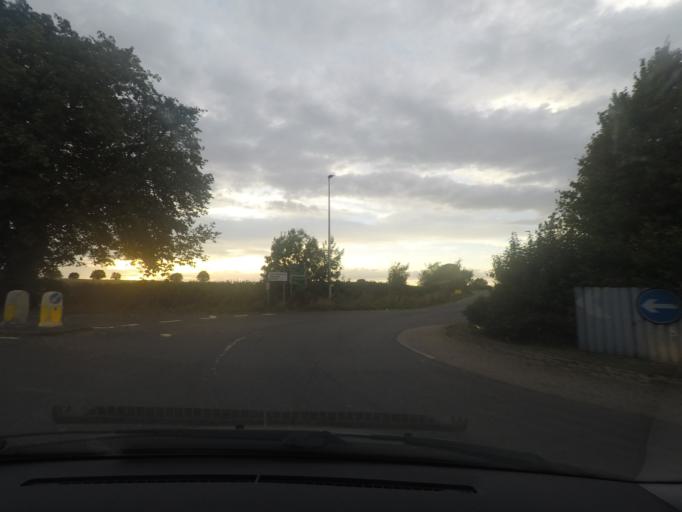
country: GB
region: England
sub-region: North East Lincolnshire
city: Wold Newton
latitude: 53.4876
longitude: -0.1296
